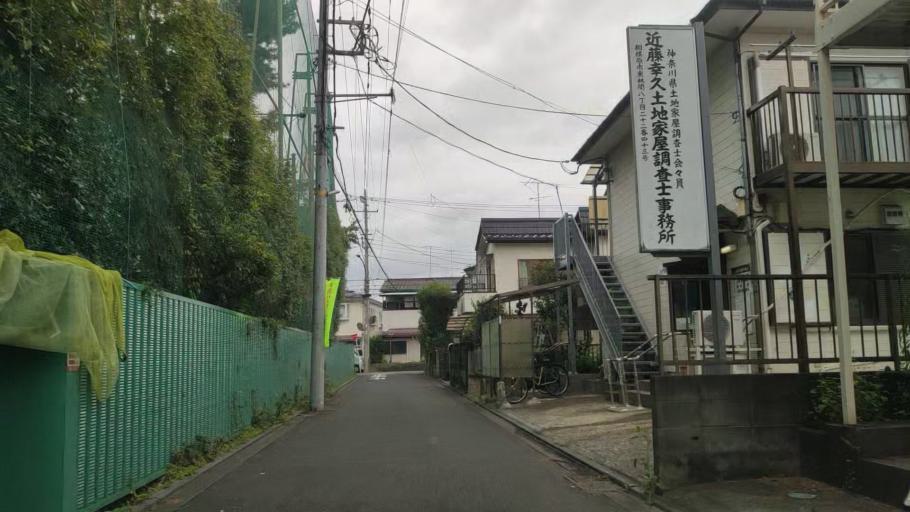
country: JP
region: Tokyo
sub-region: Machida-shi
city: Machida
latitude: 35.5127
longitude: 139.4384
